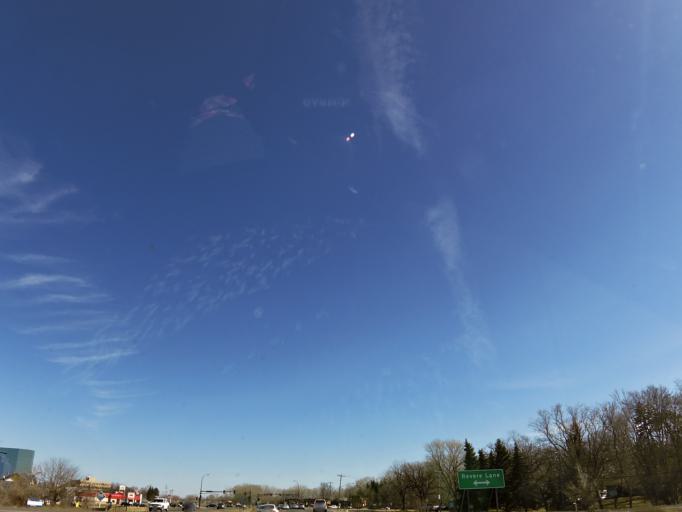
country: US
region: Minnesota
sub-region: Hennepin County
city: Plymouth
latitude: 44.9854
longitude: -93.4138
